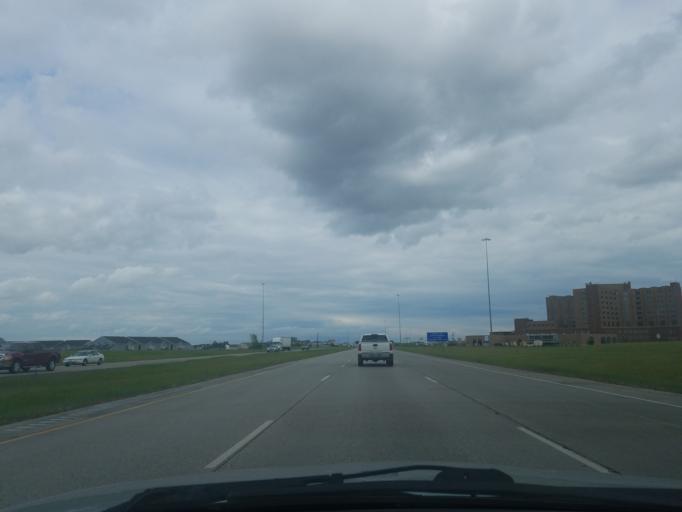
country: US
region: North Dakota
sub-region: Cass County
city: West Fargo
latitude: 46.8475
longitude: -96.8823
